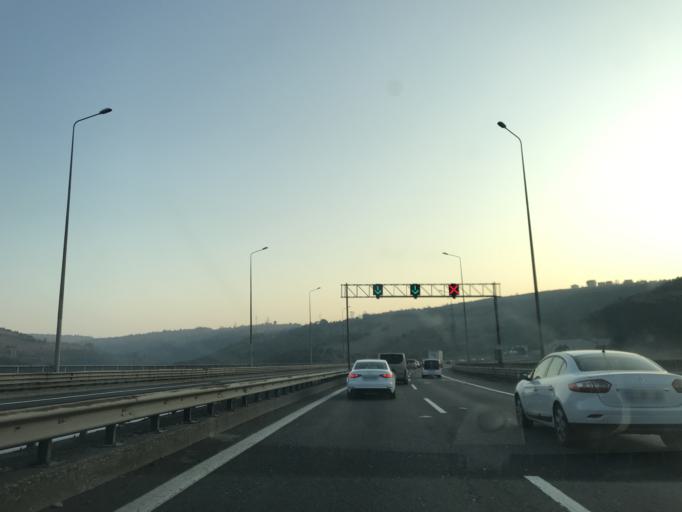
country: TR
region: Kocaeli
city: Izmit
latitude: 40.7780
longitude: 29.8827
